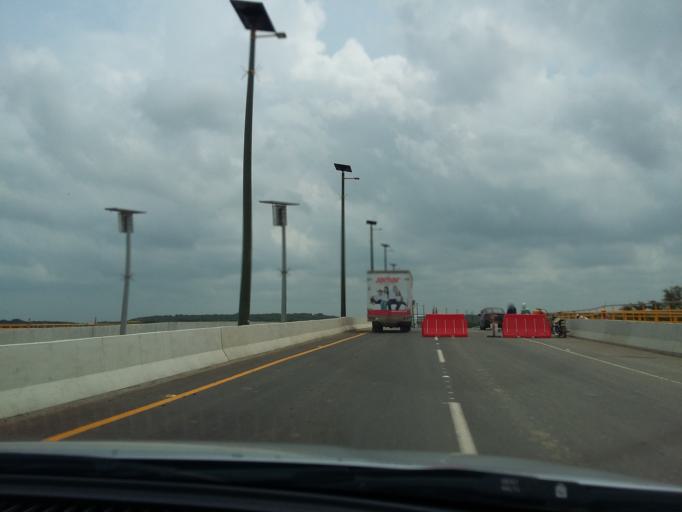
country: CO
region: Bolivar
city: Cartagena
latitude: 10.4978
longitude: -75.4776
